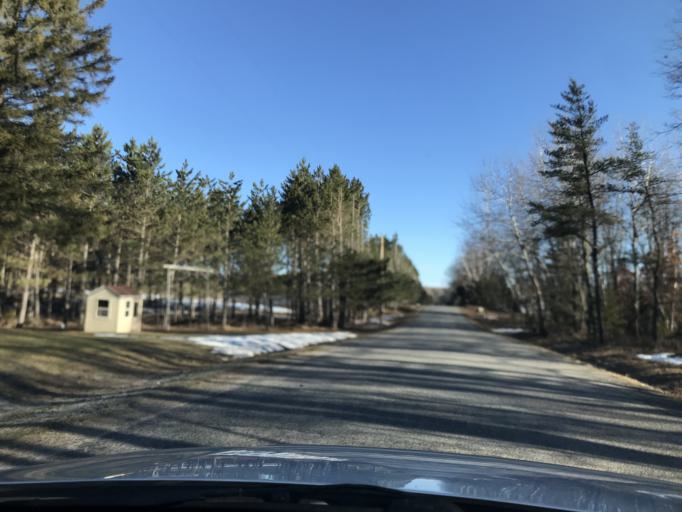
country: US
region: Wisconsin
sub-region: Marinette County
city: Niagara
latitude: 45.3590
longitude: -88.0296
